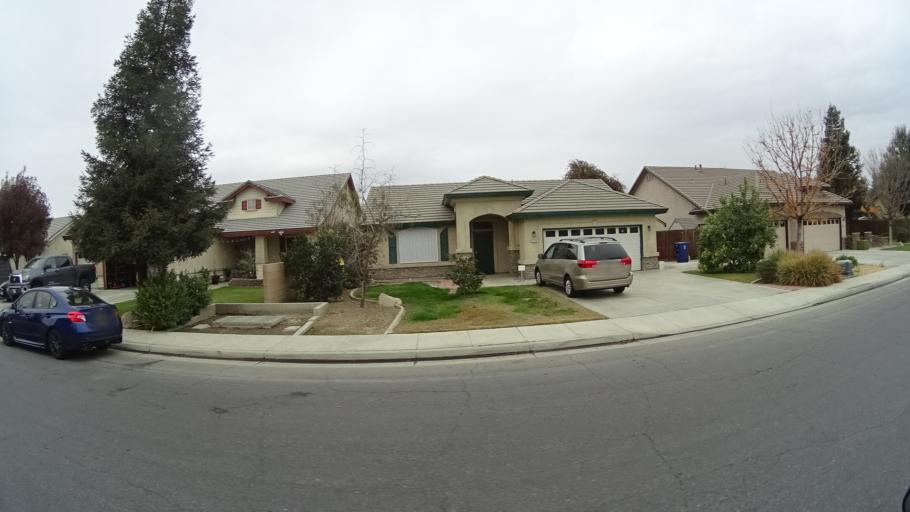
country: US
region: California
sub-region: Kern County
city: Greenfield
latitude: 35.2820
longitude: -119.0328
